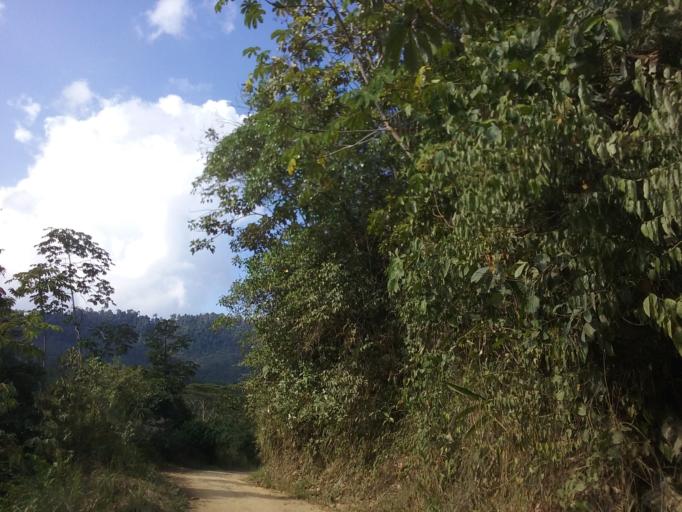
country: CO
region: Tolima
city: Libano
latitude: 4.8875
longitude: -75.0279
